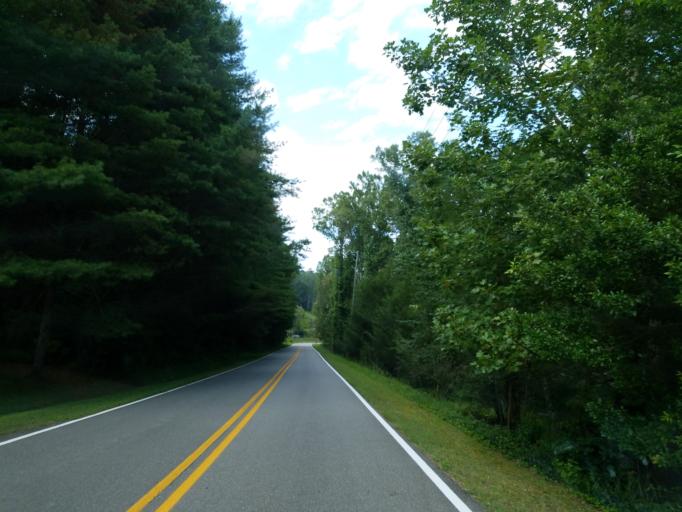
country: US
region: Georgia
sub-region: Gilmer County
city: Ellijay
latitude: 34.7653
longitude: -84.4214
